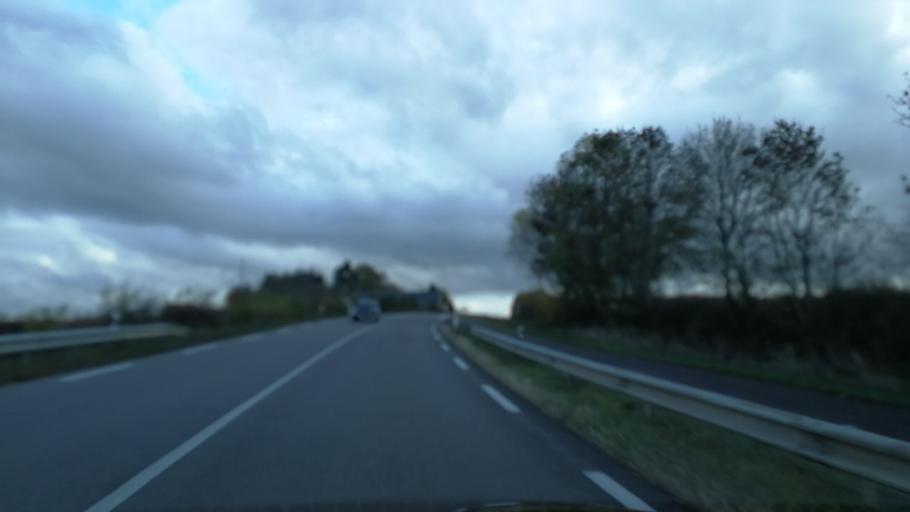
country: FR
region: Bourgogne
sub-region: Departement de la Cote-d'Or
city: Saulieu
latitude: 47.2699
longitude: 4.2542
